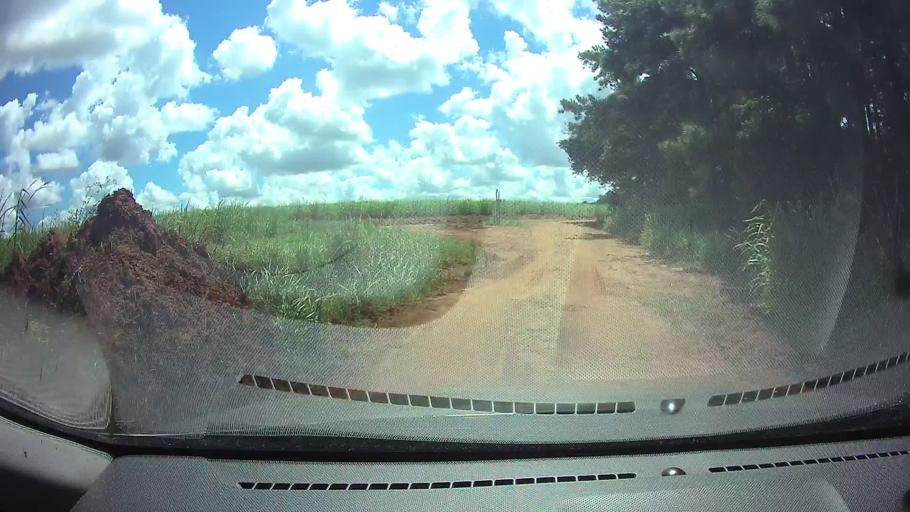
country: PY
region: Paraguari
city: La Colmena
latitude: -25.9523
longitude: -56.7745
